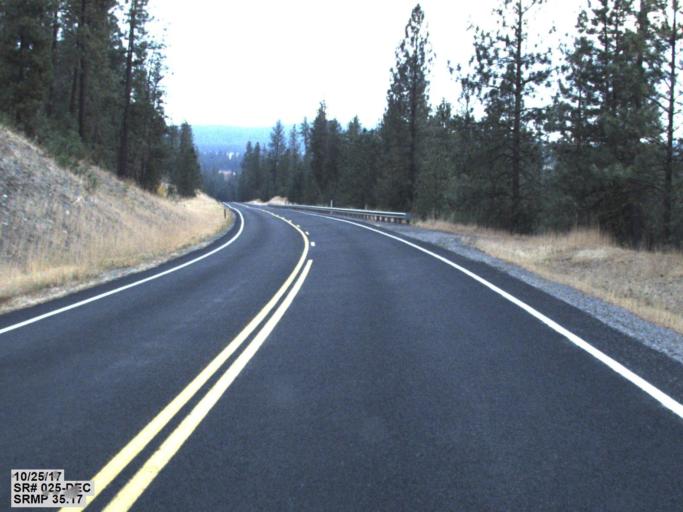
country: US
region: Washington
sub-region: Lincoln County
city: Davenport
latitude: 48.0374
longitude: -118.2293
